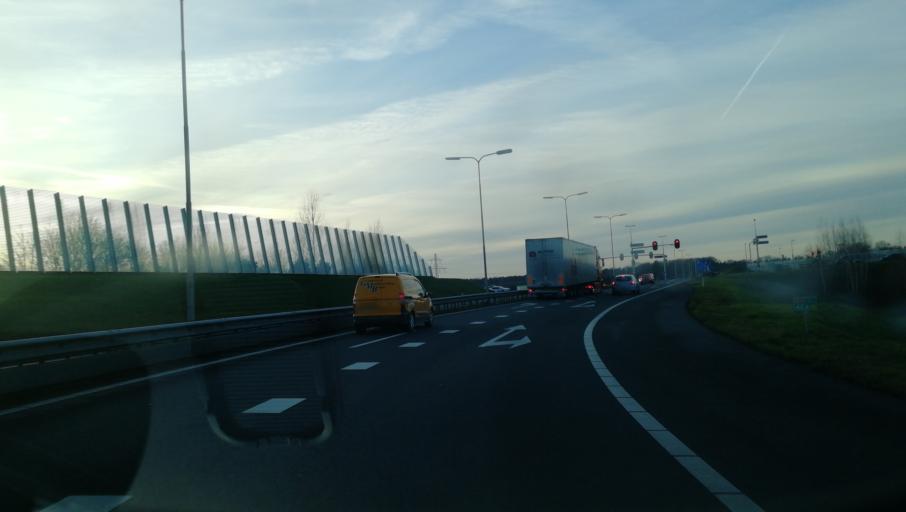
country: NL
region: Limburg
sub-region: Gemeente Venlo
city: Tegelen
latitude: 51.3630
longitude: 6.1255
